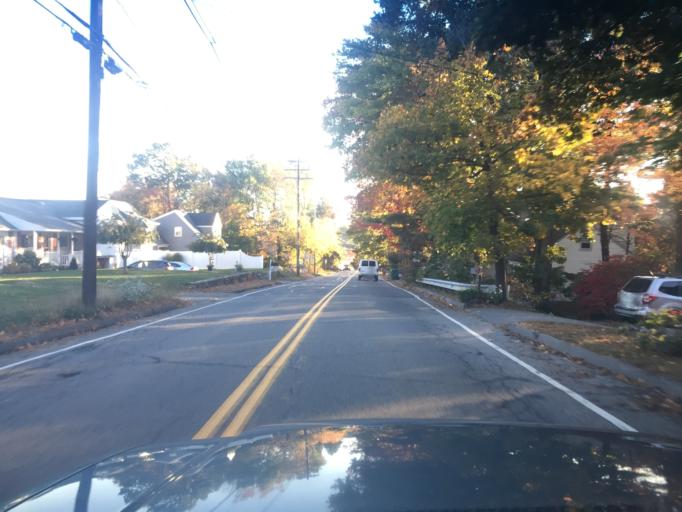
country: US
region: Massachusetts
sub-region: Middlesex County
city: Hudson
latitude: 42.3733
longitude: -71.5537
